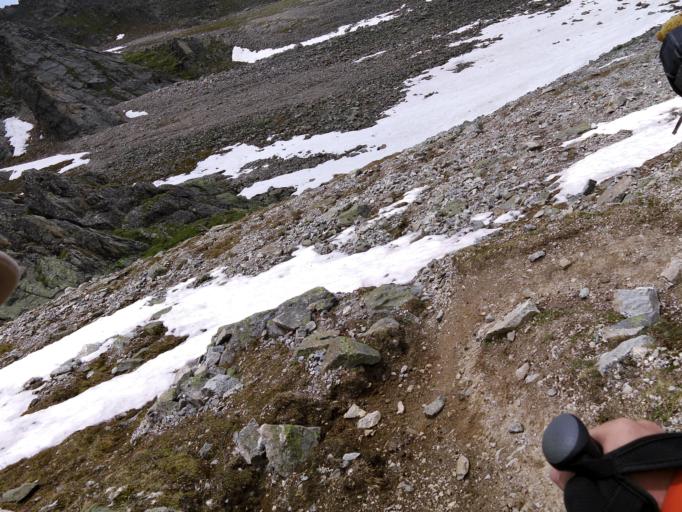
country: AT
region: Tyrol
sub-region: Politischer Bezirk Innsbruck Land
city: Neustift im Stubaital
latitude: 47.0699
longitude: 11.2068
